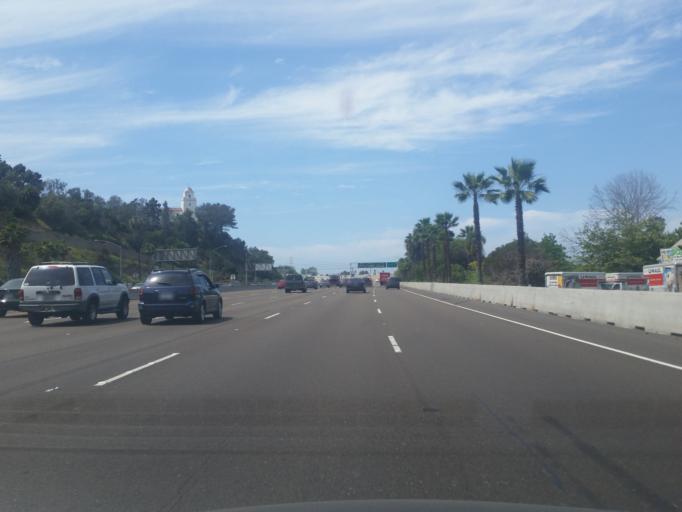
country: US
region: California
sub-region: San Diego County
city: San Diego
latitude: 32.7600
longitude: -117.1891
